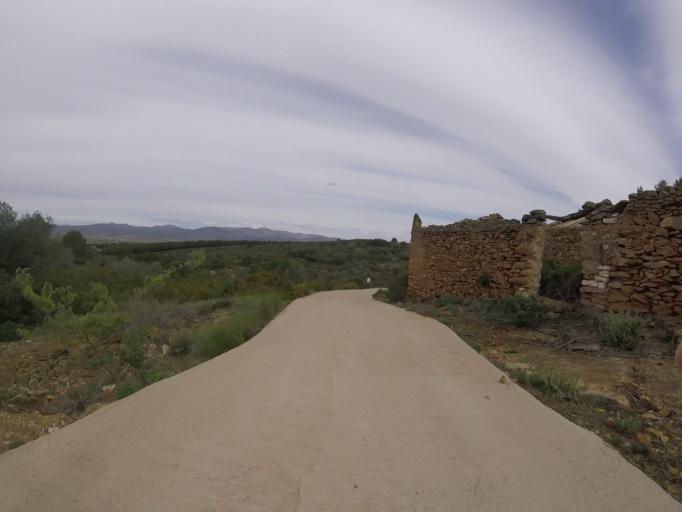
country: ES
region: Valencia
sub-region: Provincia de Castello
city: Cabanes
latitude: 40.1934
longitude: 0.0770
